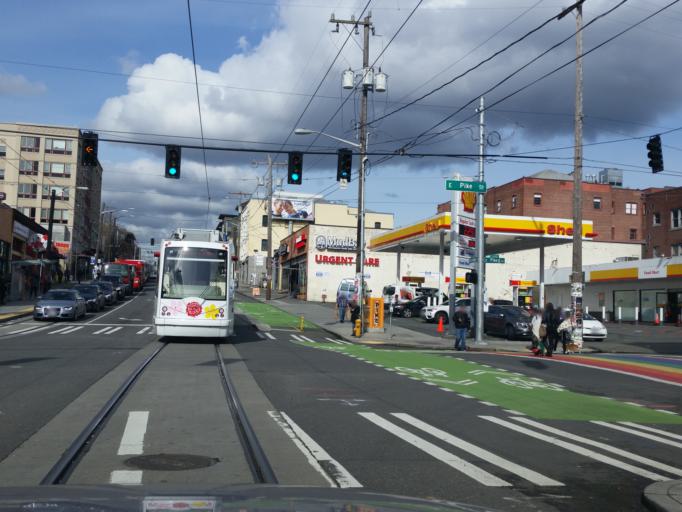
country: US
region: Washington
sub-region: King County
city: Seattle
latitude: 47.6139
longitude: -122.3208
